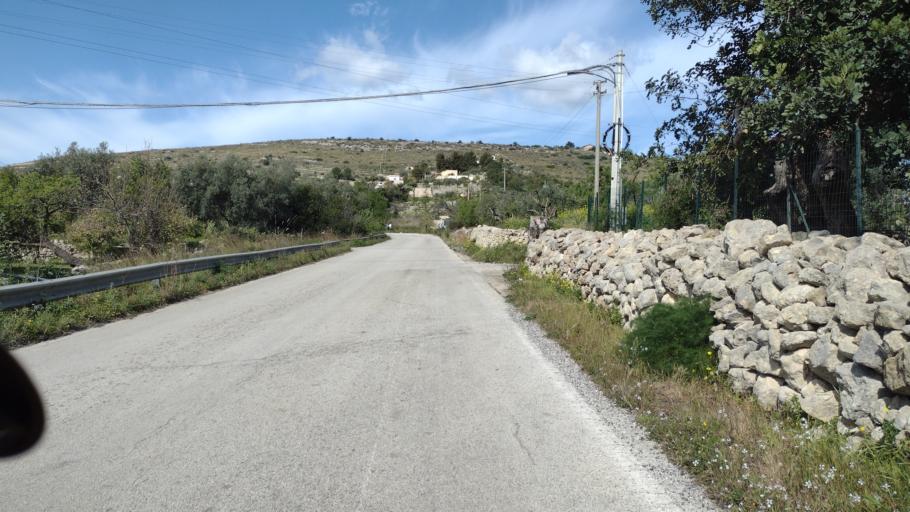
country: IT
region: Sicily
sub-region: Provincia di Siracusa
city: Noto
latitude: 36.9073
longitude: 15.0308
